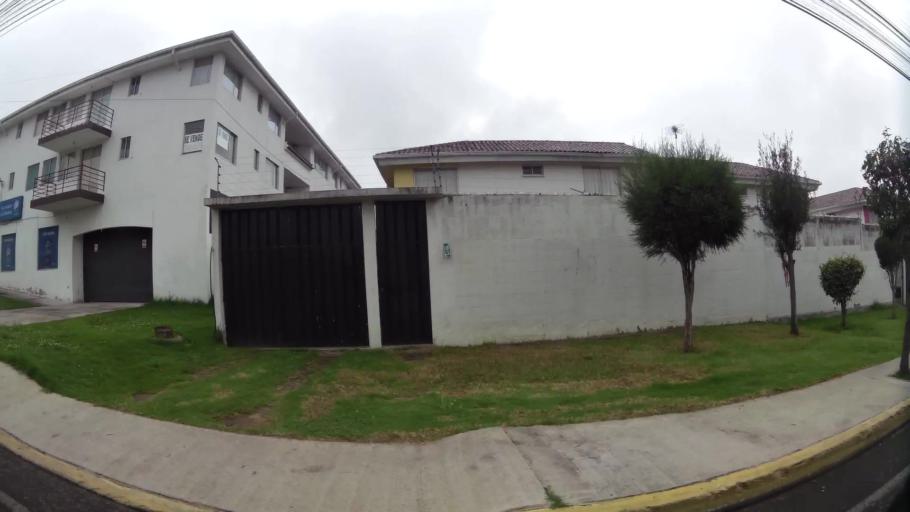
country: EC
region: Pichincha
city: Quito
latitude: -0.2646
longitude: -78.4750
